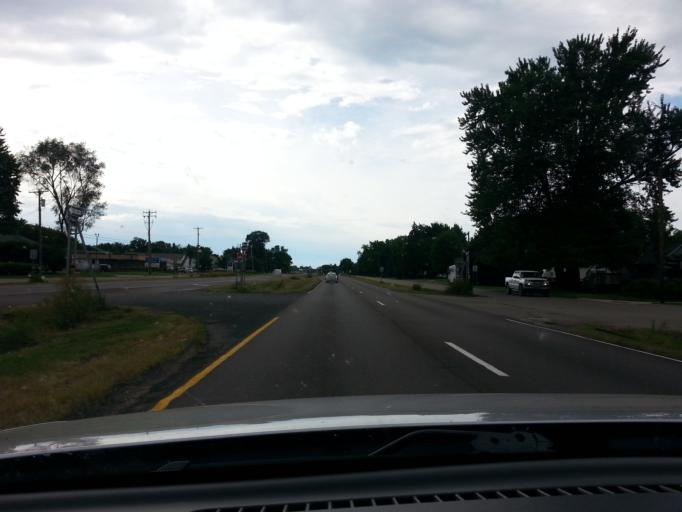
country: US
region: Minnesota
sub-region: Dakota County
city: Farmington
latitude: 44.6370
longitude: -93.1371
